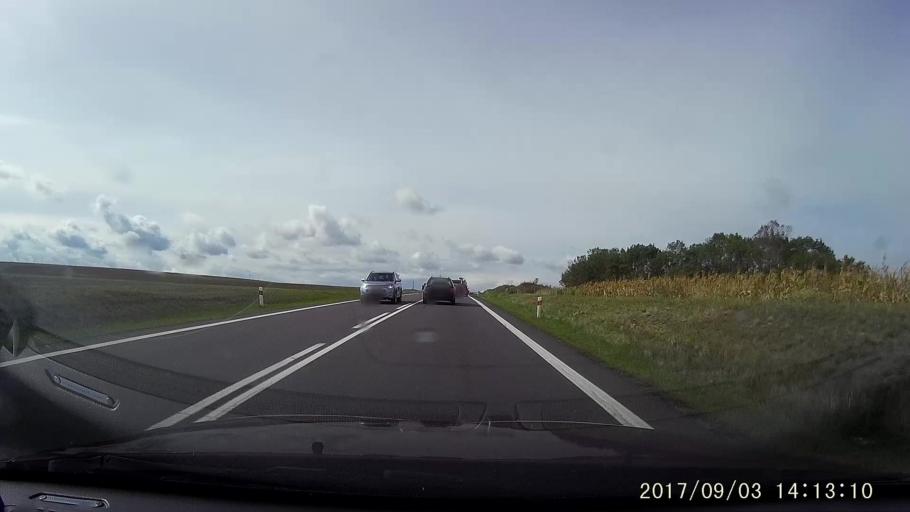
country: CZ
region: South Moravian
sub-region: Okres Znojmo
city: Znojmo
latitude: 48.8754
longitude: 16.0198
